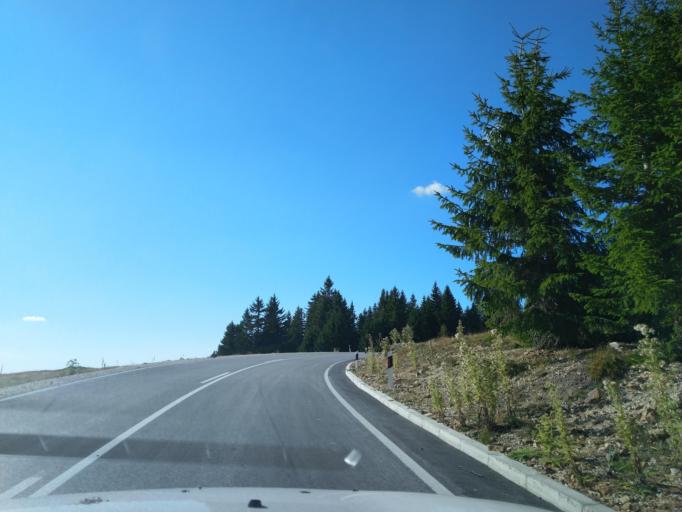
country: RS
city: Sokolovica
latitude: 43.3111
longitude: 20.2952
